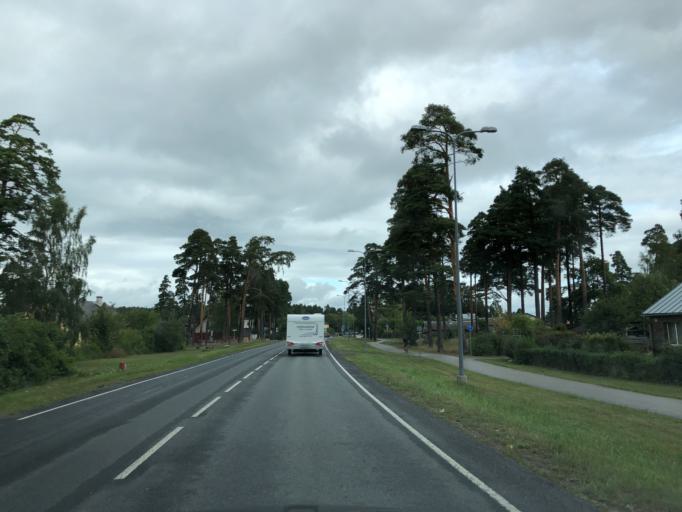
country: EE
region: Laeaene
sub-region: Haapsalu linn
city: Haapsalu
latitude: 58.9285
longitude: 23.5251
